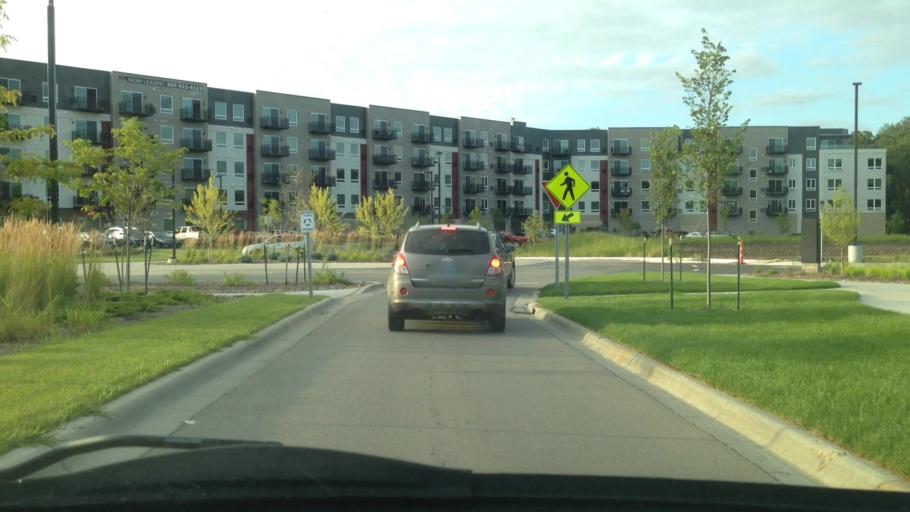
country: US
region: Minnesota
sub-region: Olmsted County
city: Rochester
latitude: 44.0007
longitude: -92.4749
